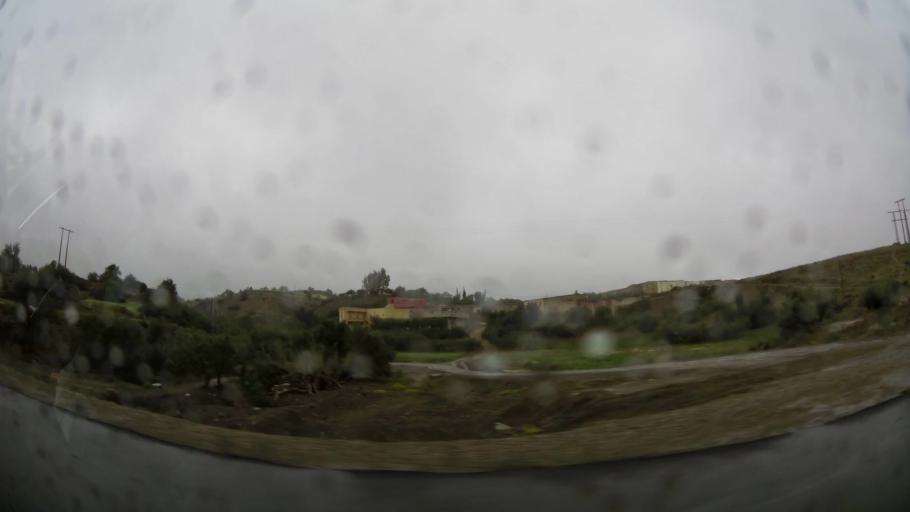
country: MA
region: Taza-Al Hoceima-Taounate
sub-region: Taza
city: Aknoul
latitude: 34.7939
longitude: -3.7478
